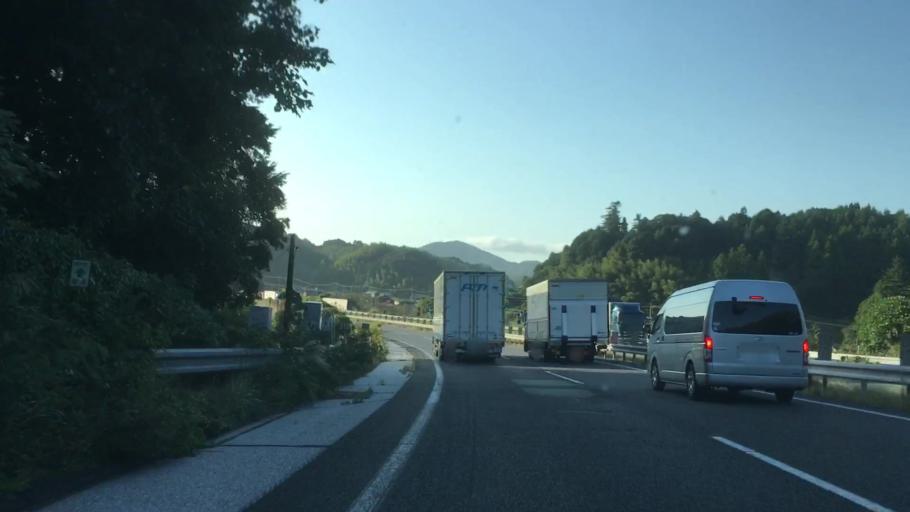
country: JP
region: Yamaguchi
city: Onoda
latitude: 34.1146
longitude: 131.1322
